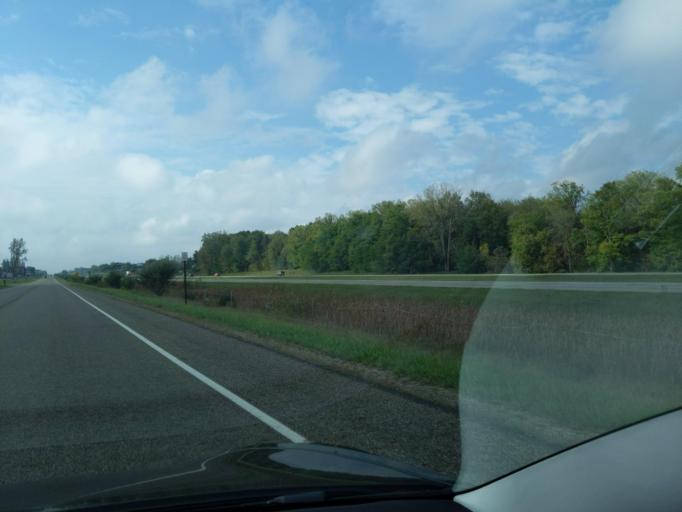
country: US
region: Michigan
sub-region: Eaton County
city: Potterville
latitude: 42.5994
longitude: -84.7792
